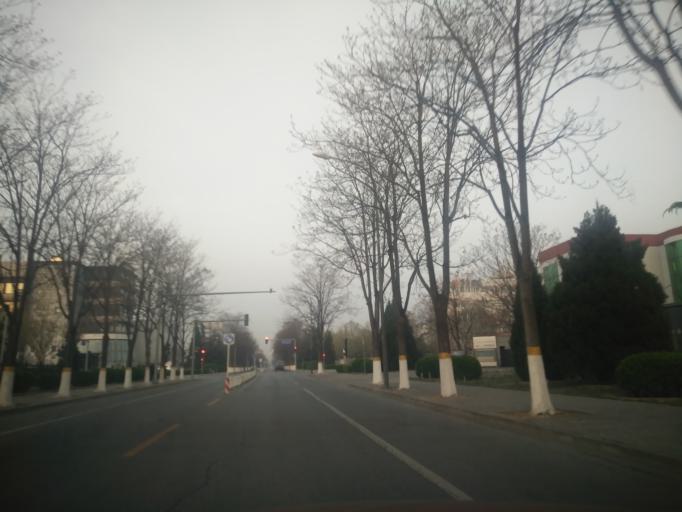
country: CN
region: Beijing
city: Jiugong
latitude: 39.8037
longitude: 116.5103
